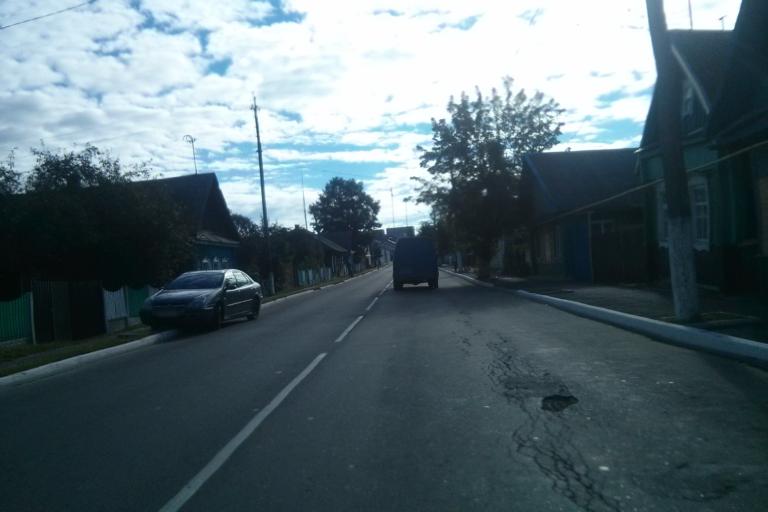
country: BY
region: Minsk
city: Chervyen'
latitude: 53.7160
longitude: 28.4128
